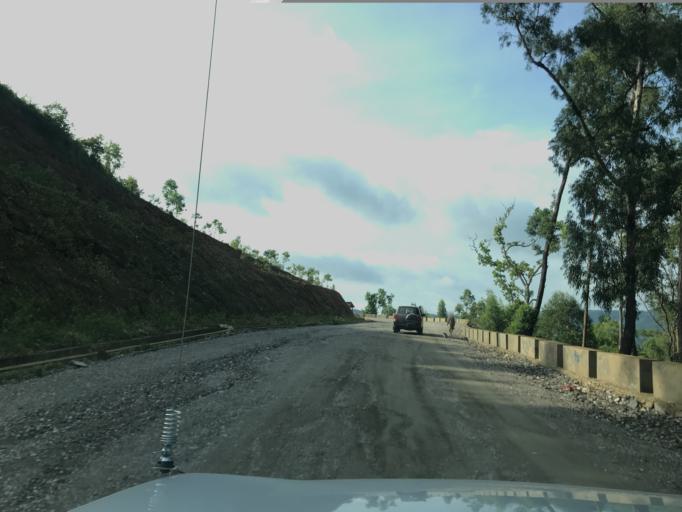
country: TL
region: Aileu
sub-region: Aileu Villa
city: Aileu
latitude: -8.6632
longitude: 125.5423
